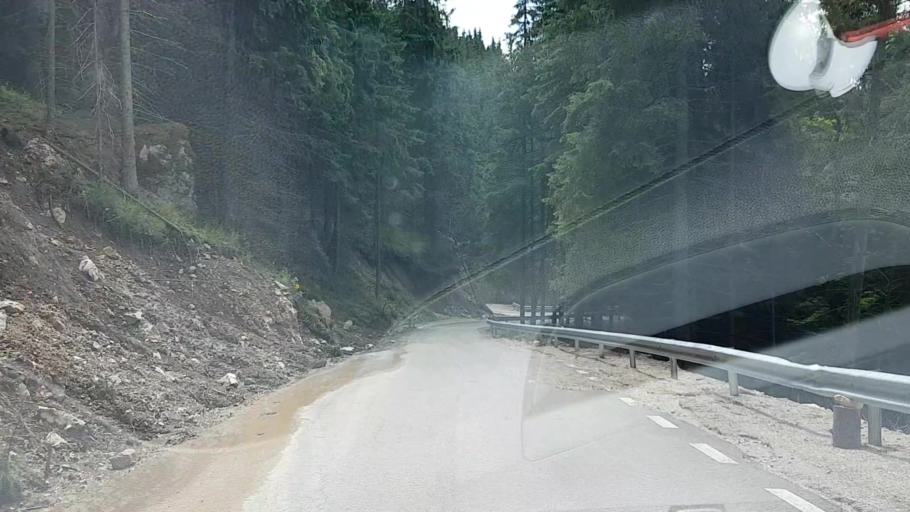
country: RO
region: Suceava
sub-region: Municipiul Campulung Moldovenesc
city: Campulung Moldovenesc
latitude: 47.4459
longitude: 25.5562
